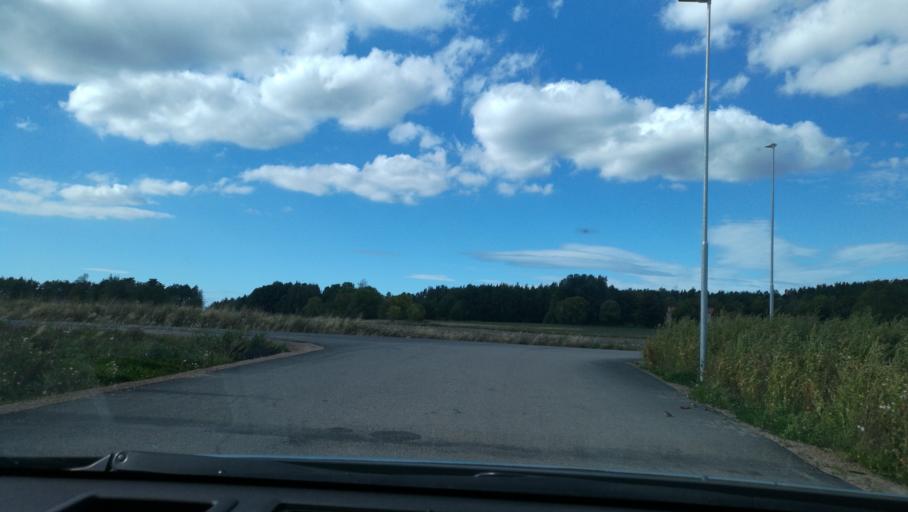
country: SE
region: Vaestra Goetaland
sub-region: Mariestads Kommun
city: Mariestad
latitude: 58.6783
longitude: 13.8149
